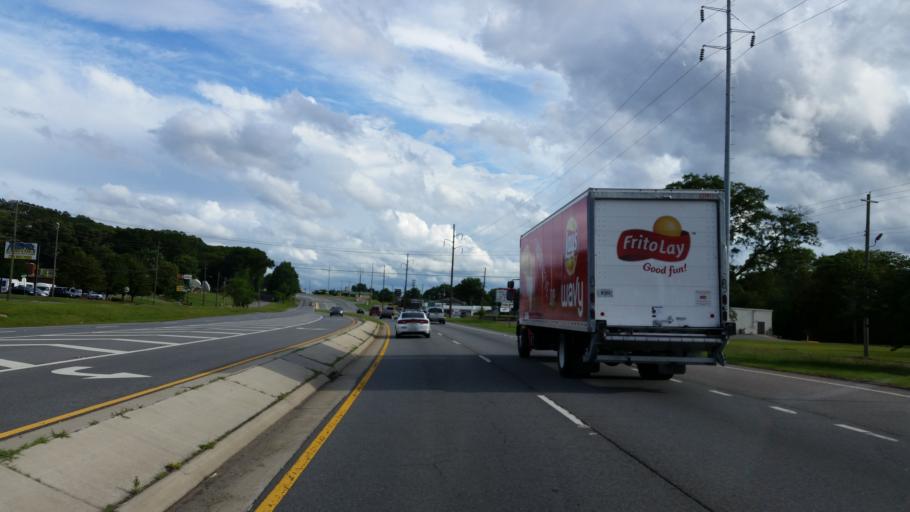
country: US
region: Georgia
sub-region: Bartow County
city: Cartersville
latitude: 34.1661
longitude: -84.7889
